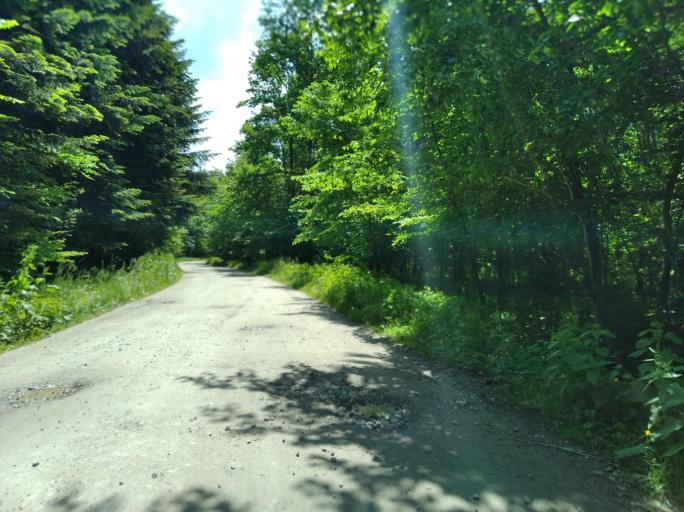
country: PL
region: Subcarpathian Voivodeship
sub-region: Powiat ropczycko-sedziszowski
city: Zagorzyce
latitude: 49.9727
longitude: 21.6861
